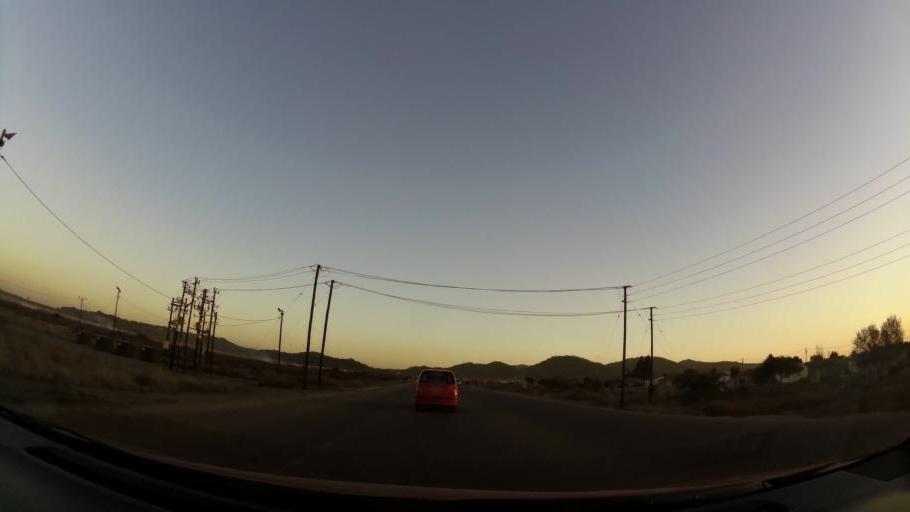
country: ZA
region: North-West
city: Ga-Rankuwa
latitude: -25.5900
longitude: 28.0440
